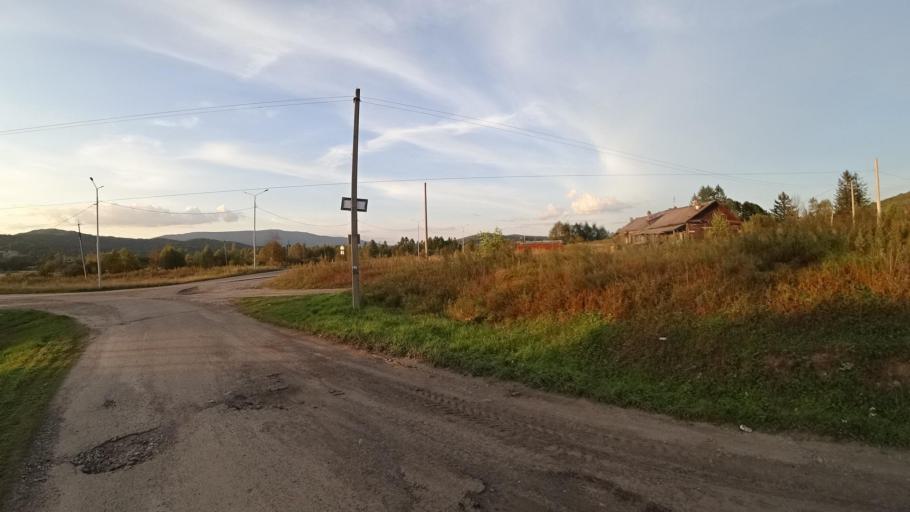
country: RU
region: Jewish Autonomous Oblast
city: Kul'dur
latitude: 49.1987
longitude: 131.6325
